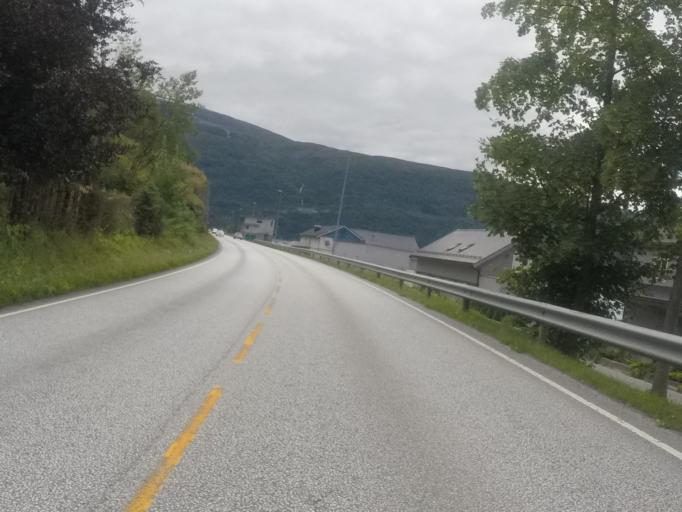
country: NO
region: Sogn og Fjordane
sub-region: Stryn
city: Stryn
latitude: 61.8970
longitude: 6.7064
